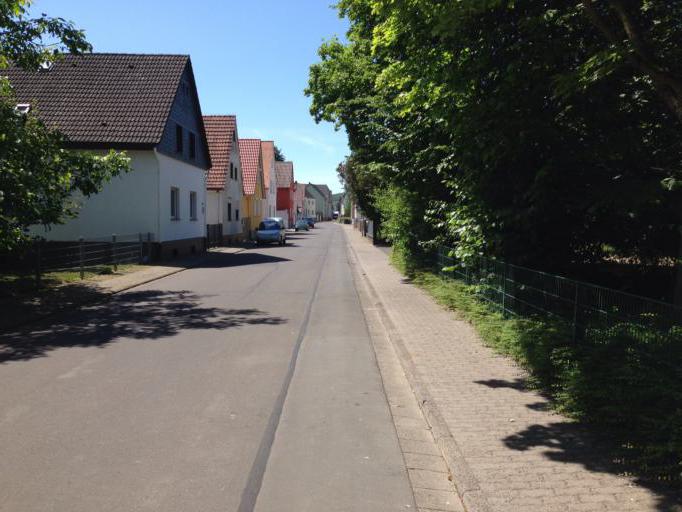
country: DE
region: Hesse
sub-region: Regierungsbezirk Giessen
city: Alten Buseck
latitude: 50.6192
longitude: 8.7603
